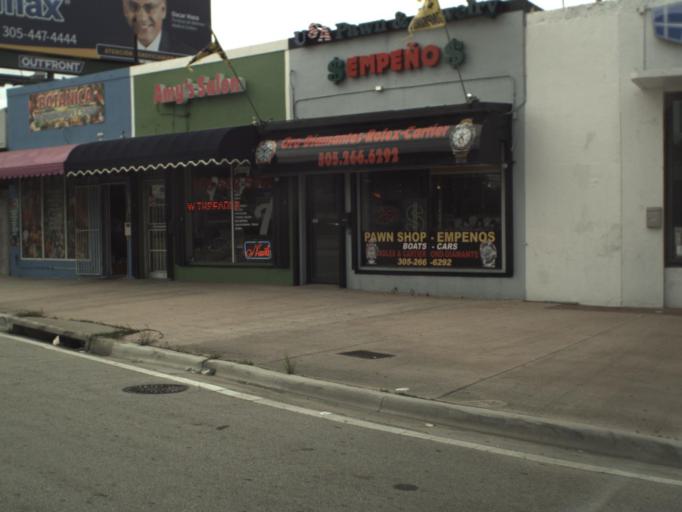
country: US
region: Florida
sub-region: Miami-Dade County
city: Flagami
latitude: 25.7628
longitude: -80.3151
